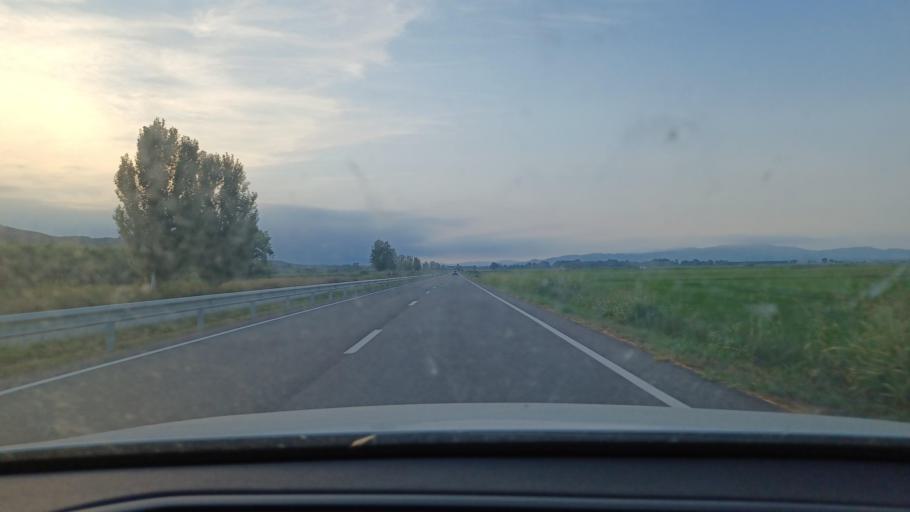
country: ES
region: Catalonia
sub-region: Provincia de Tarragona
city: Sant Carles de la Rapita
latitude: 40.6502
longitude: 0.5969
